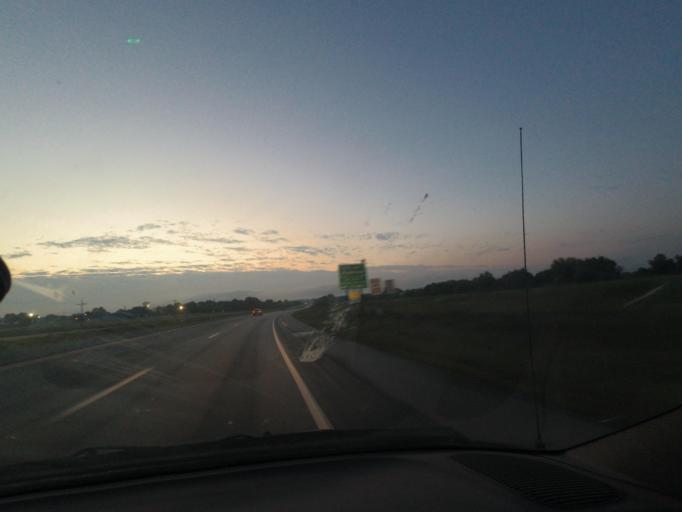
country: US
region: Missouri
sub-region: Linn County
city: Brookfield
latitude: 39.7797
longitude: -93.1039
